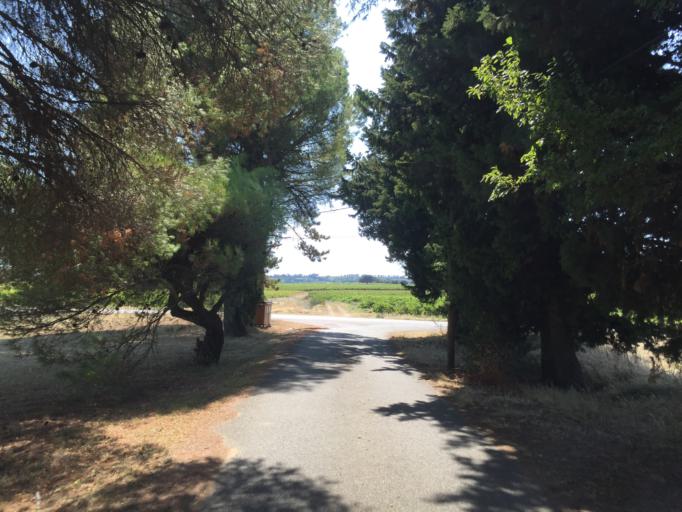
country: FR
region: Provence-Alpes-Cote d'Azur
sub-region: Departement du Vaucluse
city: Orange
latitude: 44.1061
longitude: 4.8260
